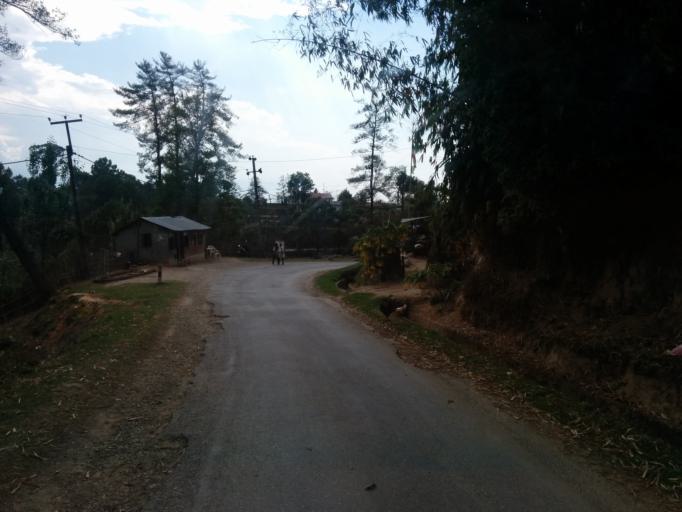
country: NP
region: Central Region
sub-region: Bagmati Zone
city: Nagarkot
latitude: 27.7118
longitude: 85.4920
